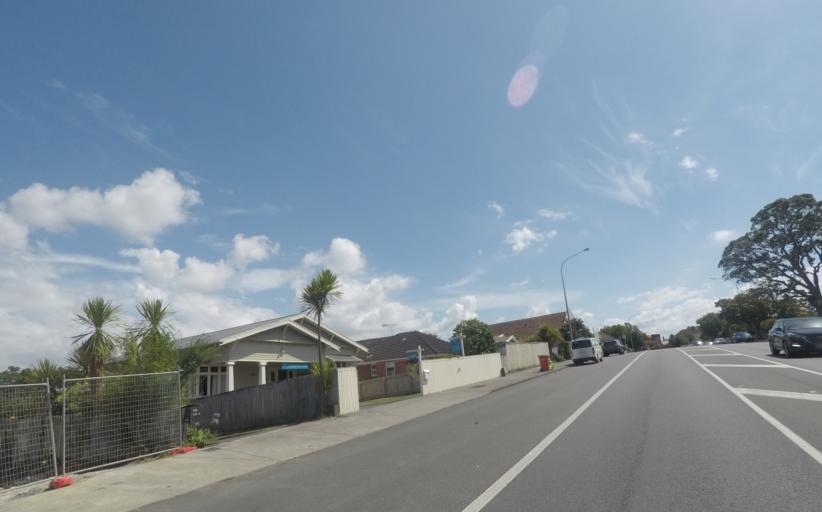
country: NZ
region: Auckland
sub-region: Auckland
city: Tamaki
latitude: -36.8800
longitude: 174.8166
